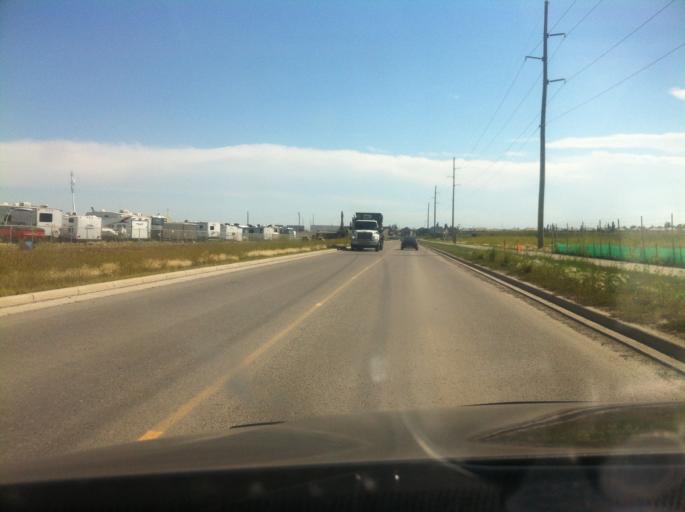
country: CA
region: Alberta
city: Calgary
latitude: 50.9611
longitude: -114.0019
